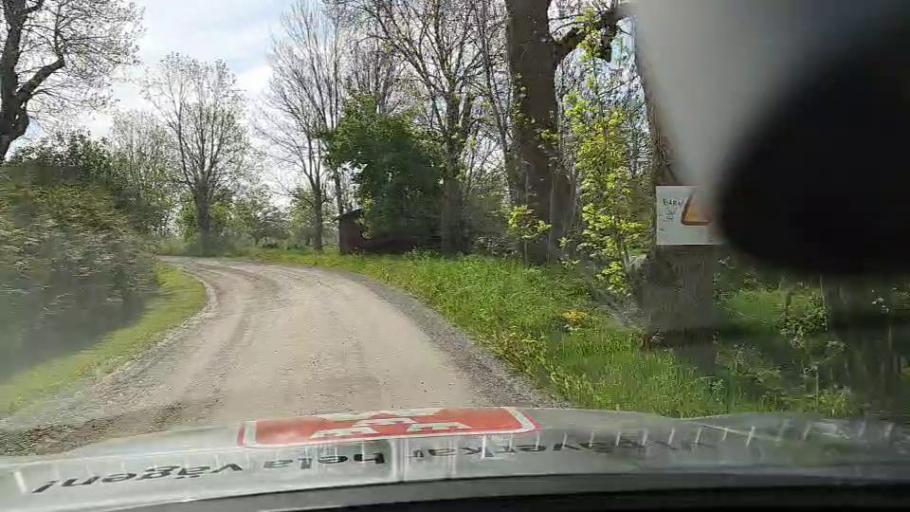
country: SE
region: Soedermanland
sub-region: Eskilstuna Kommun
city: Arla
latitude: 59.2586
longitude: 16.7925
